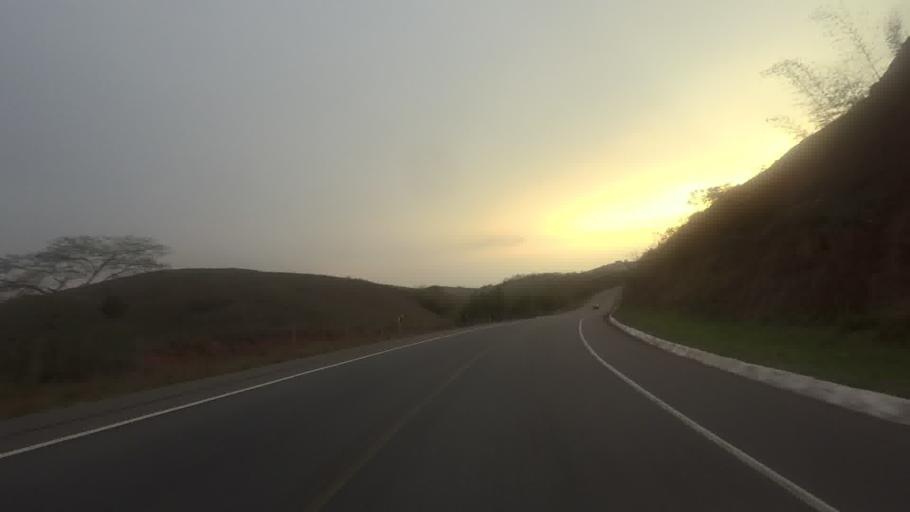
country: BR
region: Rio de Janeiro
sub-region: Carmo
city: Carmo
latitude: -21.7567
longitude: -42.4808
